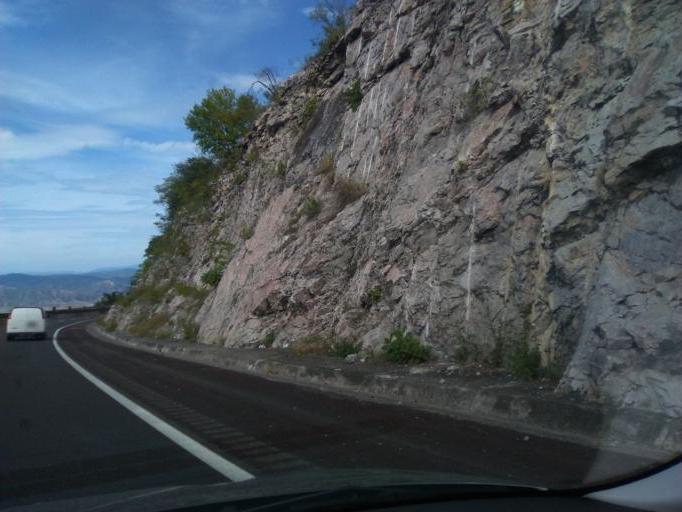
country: MX
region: Guerrero
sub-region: Eduardo Neri
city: Tlanipatla
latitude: 17.8611
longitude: -99.4062
